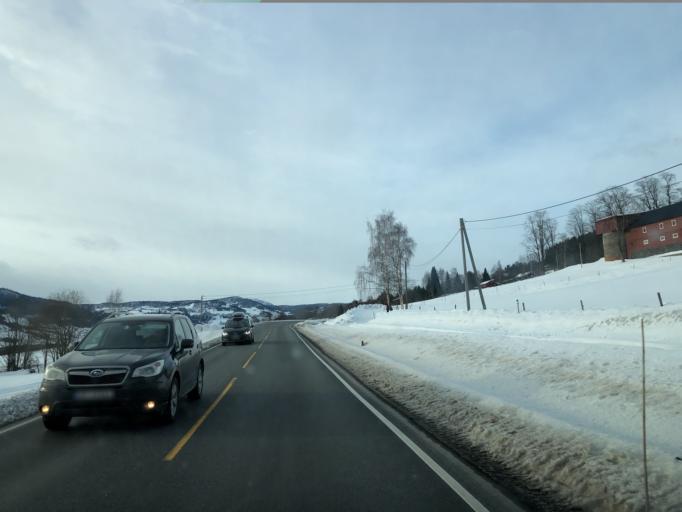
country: NO
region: Oppland
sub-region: Gausdal
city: Segalstad bru
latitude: 61.2433
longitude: 10.1967
